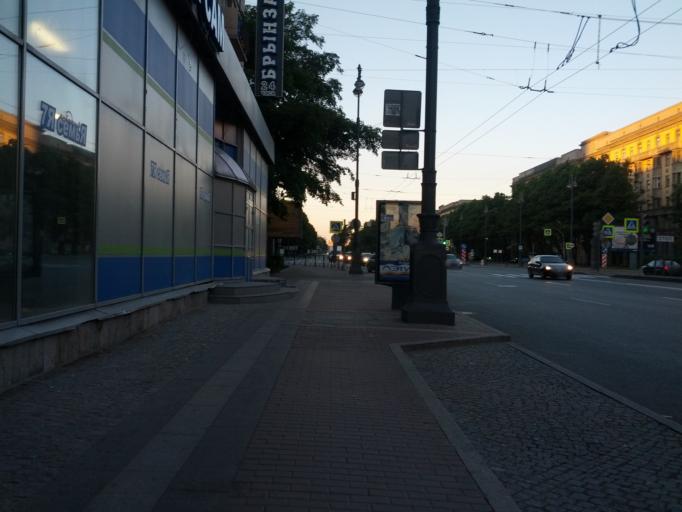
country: RU
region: St.-Petersburg
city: Admiralteisky
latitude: 59.9032
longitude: 30.3185
